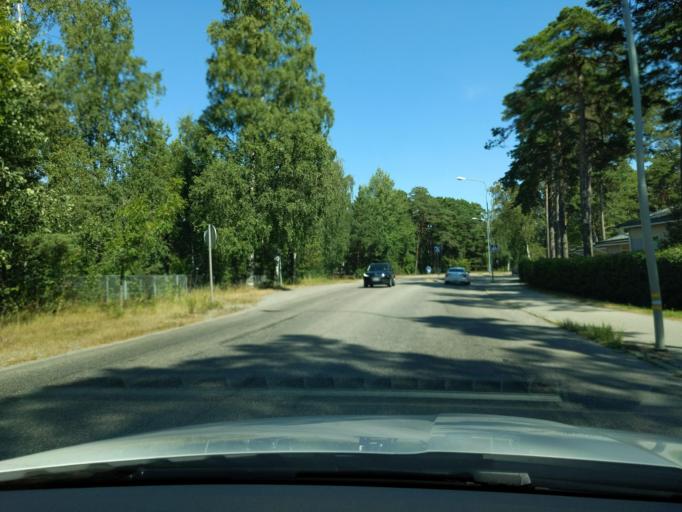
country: FI
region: Uusimaa
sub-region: Raaseporin
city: Hanko
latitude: 59.8292
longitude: 22.9861
